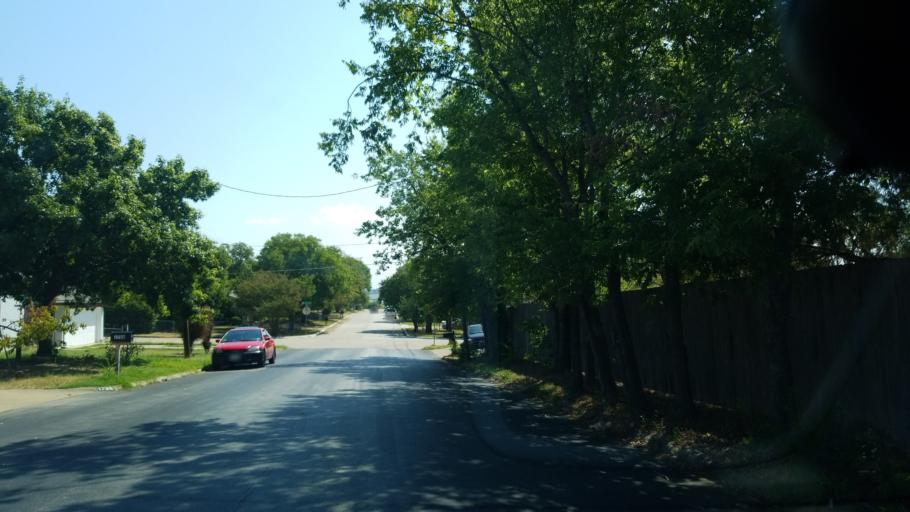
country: US
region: Texas
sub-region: Dallas County
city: Grand Prairie
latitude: 32.7079
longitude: -96.9821
